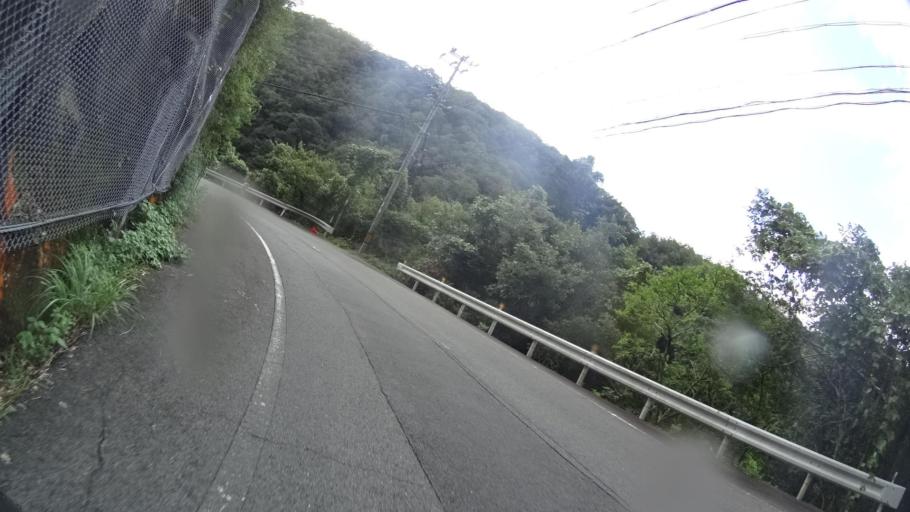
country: JP
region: Mie
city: Ueno-ebisumachi
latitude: 34.7635
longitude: 136.0032
